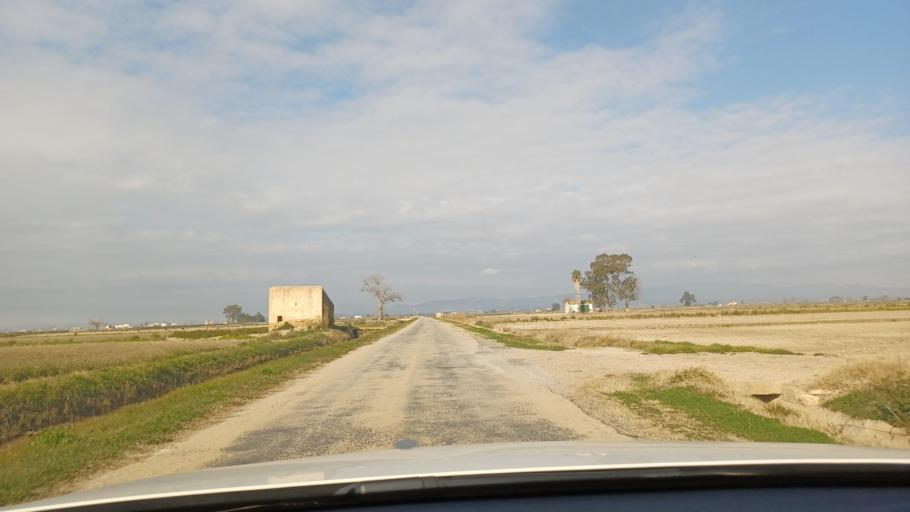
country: ES
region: Catalonia
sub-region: Provincia de Tarragona
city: Deltebre
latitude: 40.6853
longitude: 0.6546
